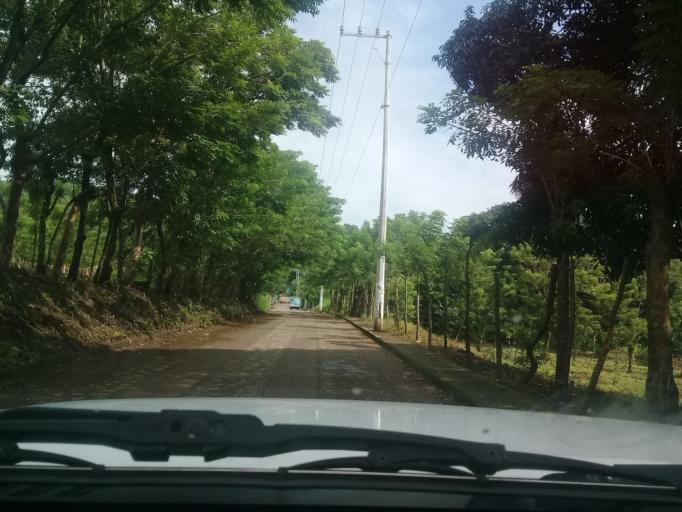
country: MX
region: Veracruz
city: Comoapan
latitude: 18.4096
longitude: -95.1607
